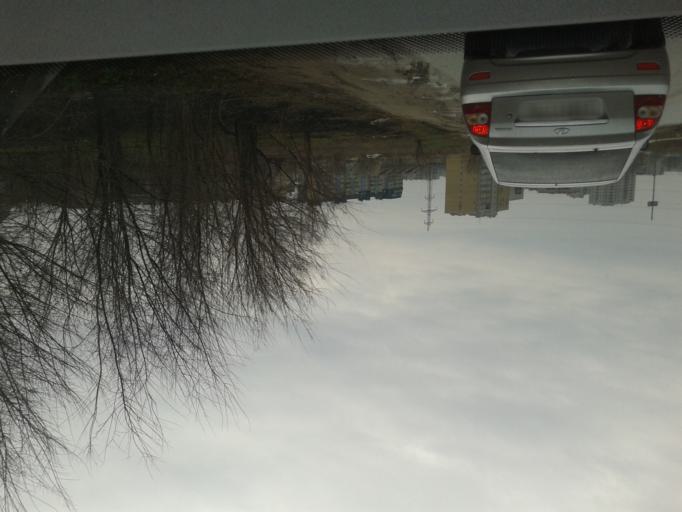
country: RU
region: Volgograd
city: Volgograd
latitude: 48.7645
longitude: 44.4978
